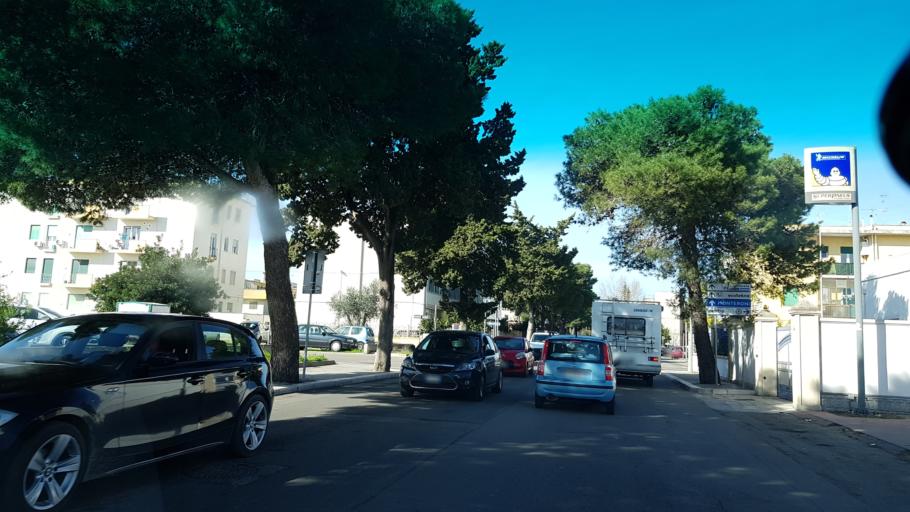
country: IT
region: Apulia
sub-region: Provincia di Lecce
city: Lecce
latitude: 40.3442
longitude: 18.1577
